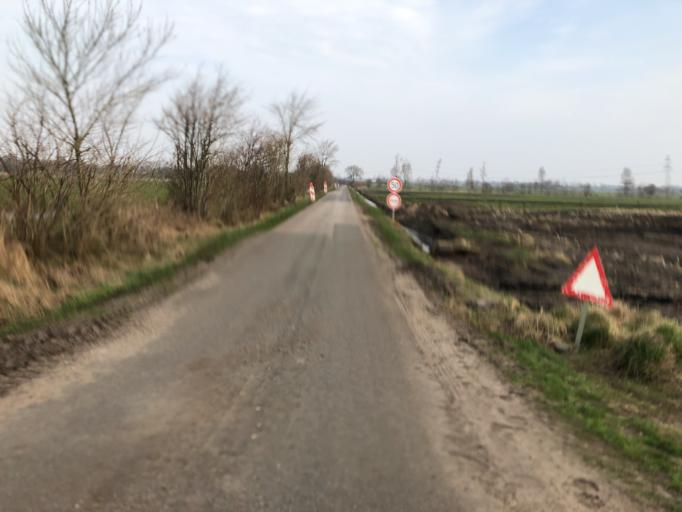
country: DE
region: Schleswig-Holstein
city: Wanderup
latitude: 54.6977
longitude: 9.3642
